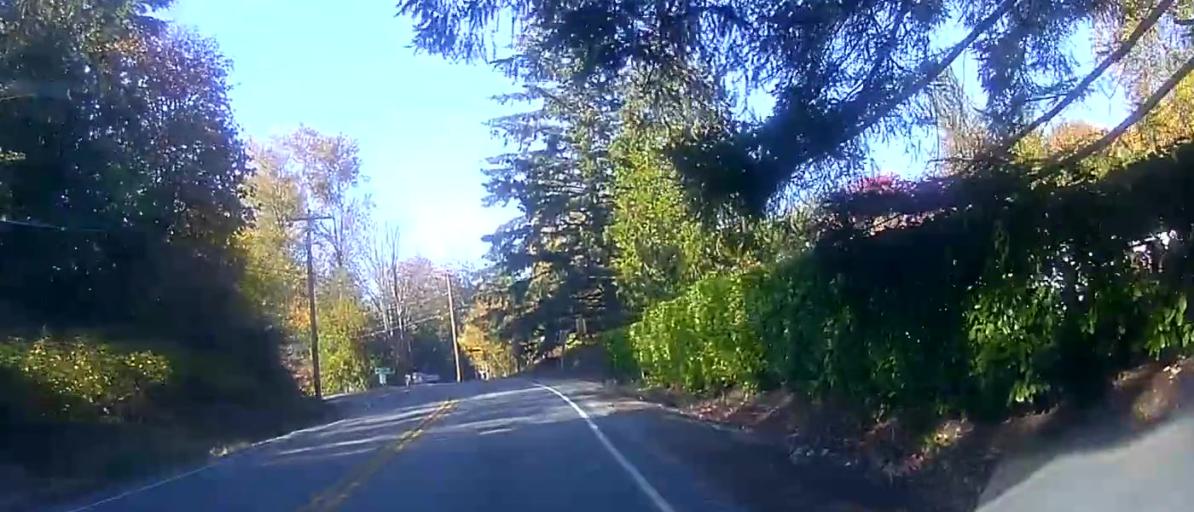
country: US
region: Washington
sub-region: Skagit County
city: Big Lake
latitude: 48.4202
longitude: -122.2688
